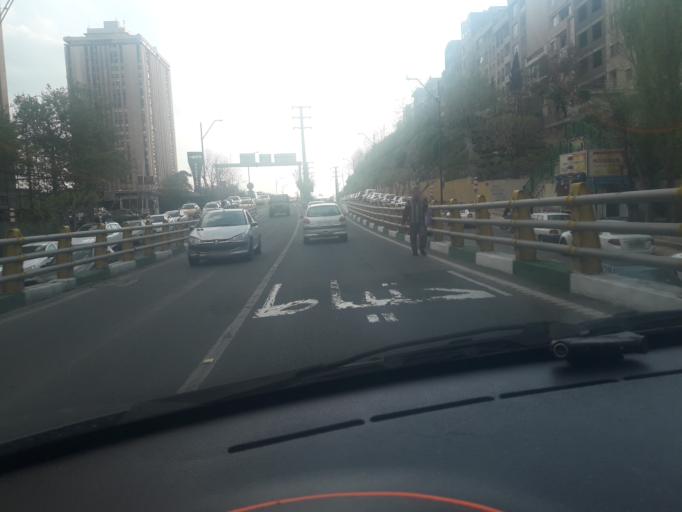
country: IR
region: Tehran
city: Tehran
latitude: 35.7460
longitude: 51.4003
